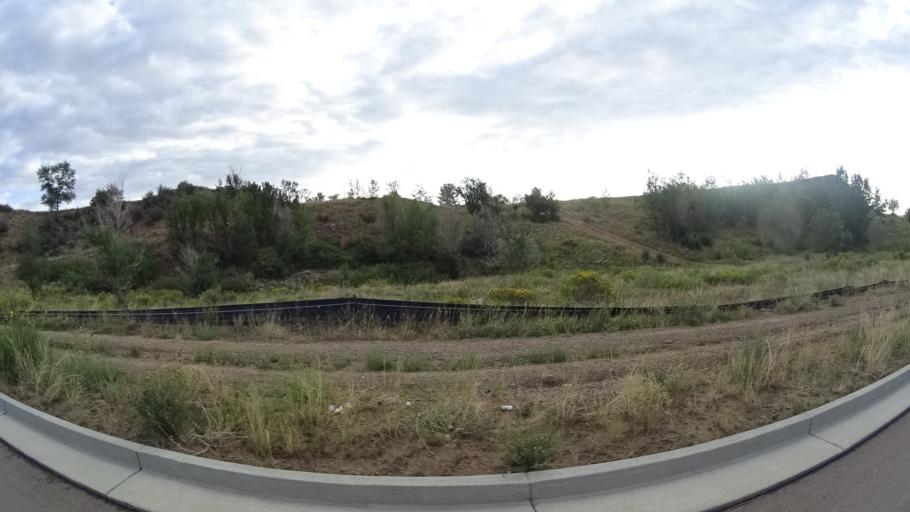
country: US
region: Colorado
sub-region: El Paso County
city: Colorado Springs
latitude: 38.8715
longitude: -104.8425
